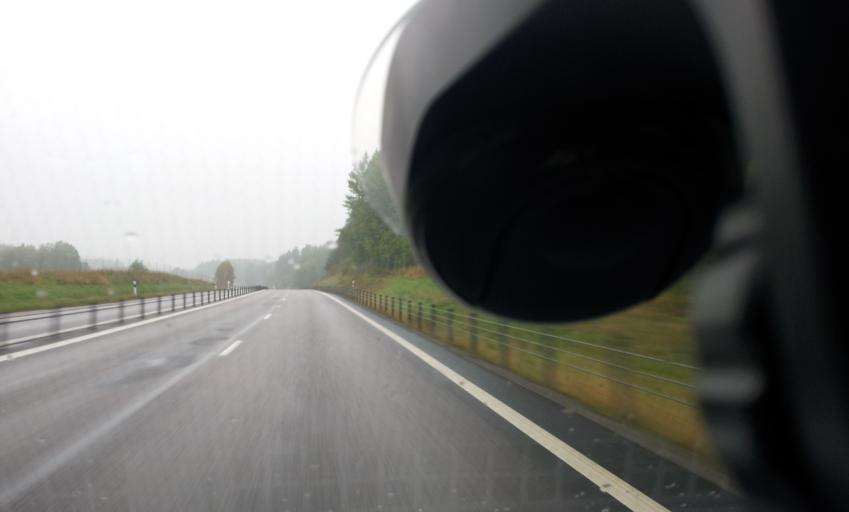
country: SE
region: OEstergoetland
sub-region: Soderkopings Kommun
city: Soederkoeping
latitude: 58.4143
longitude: 16.4001
